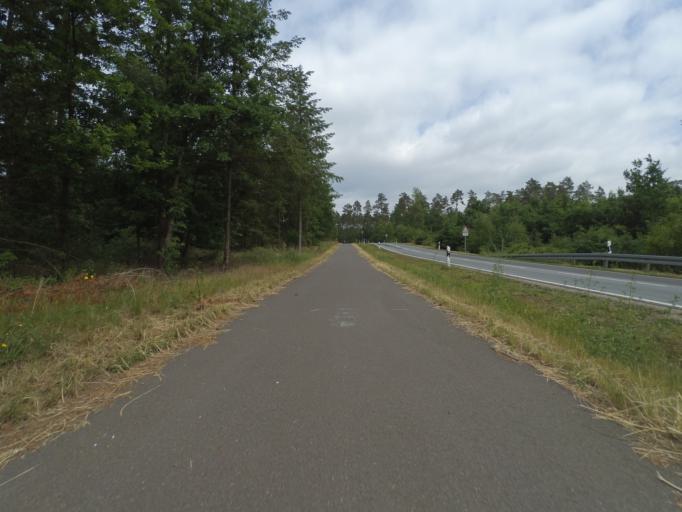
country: DE
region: Mecklenburg-Vorpommern
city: Malchow
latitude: 53.5269
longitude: 12.4661
